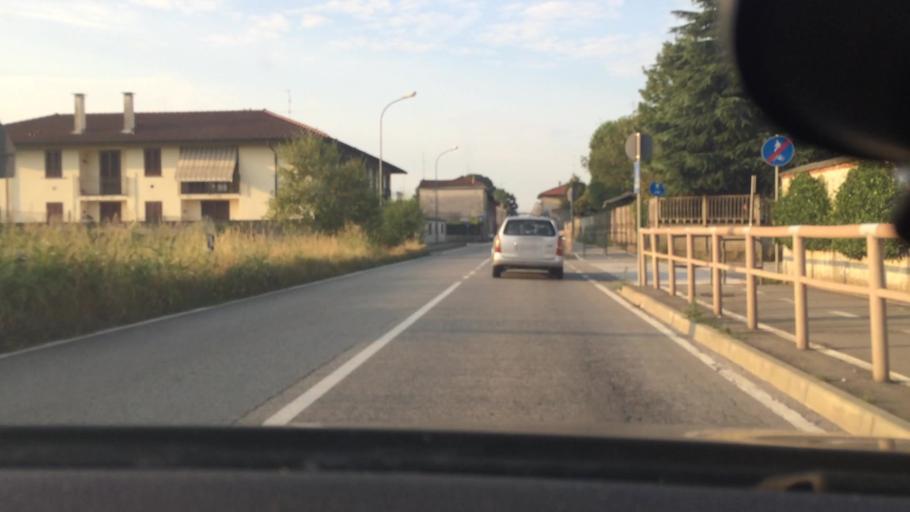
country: IT
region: Lombardy
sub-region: Citta metropolitana di Milano
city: Casorezzo
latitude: 45.5287
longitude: 8.9006
